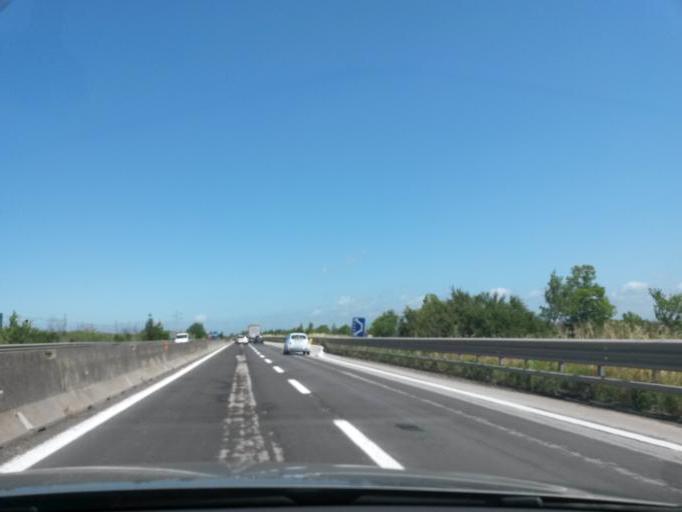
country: IT
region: Tuscany
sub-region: Provincia di Livorno
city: Donoratico
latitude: 43.2196
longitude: 10.5612
